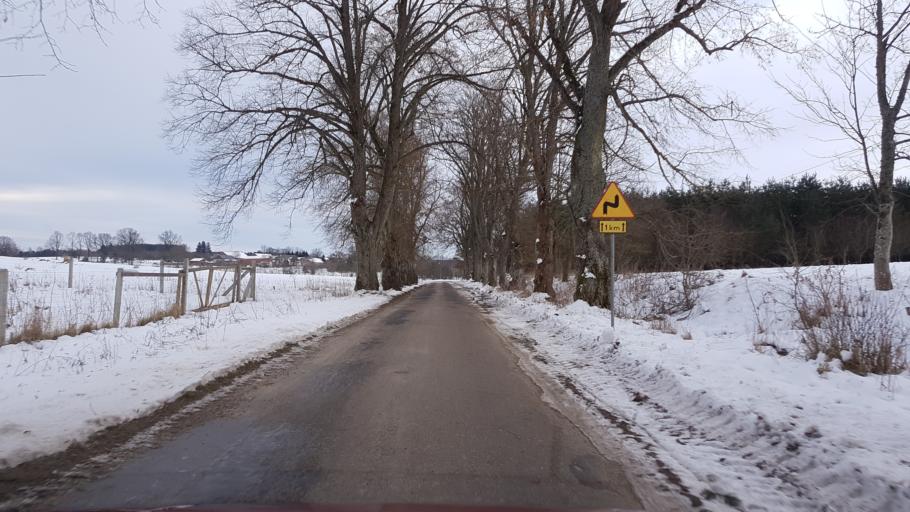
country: PL
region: West Pomeranian Voivodeship
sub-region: Powiat bialogardzki
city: Tychowo
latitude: 53.9206
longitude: 16.3521
